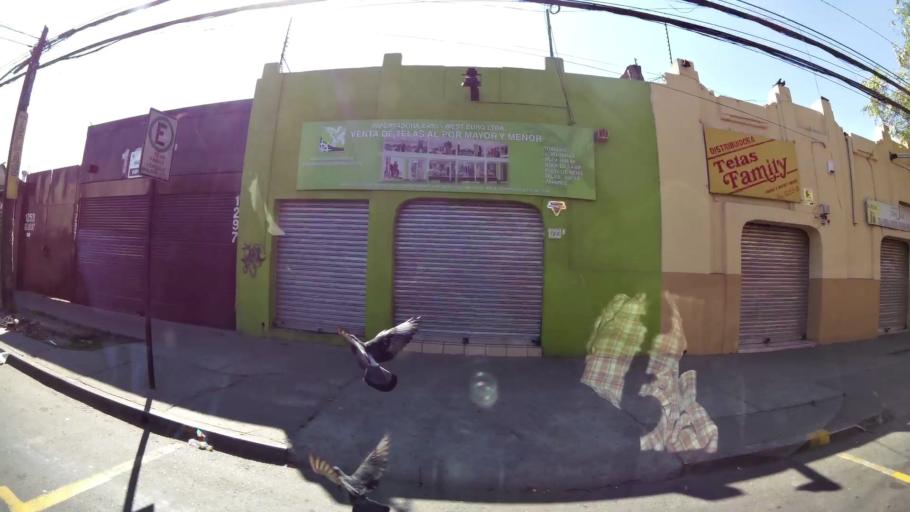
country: CL
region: Santiago Metropolitan
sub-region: Provincia de Santiago
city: Santiago
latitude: -33.4255
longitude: -70.6555
